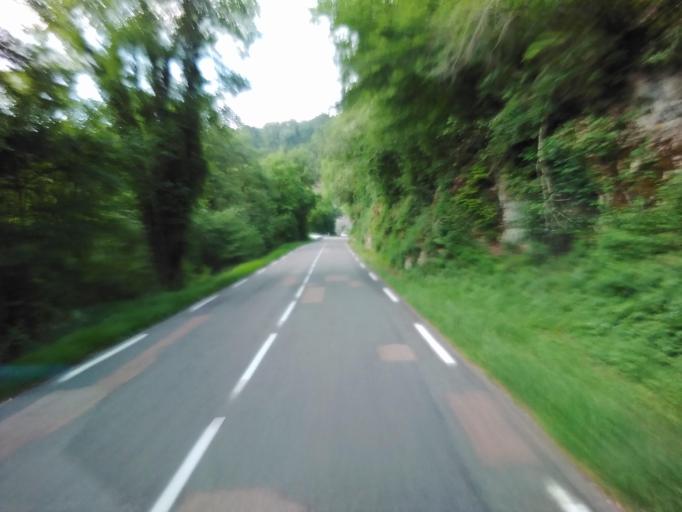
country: FR
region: Franche-Comte
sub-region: Departement du Jura
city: Arbois
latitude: 46.8748
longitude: 5.7996
